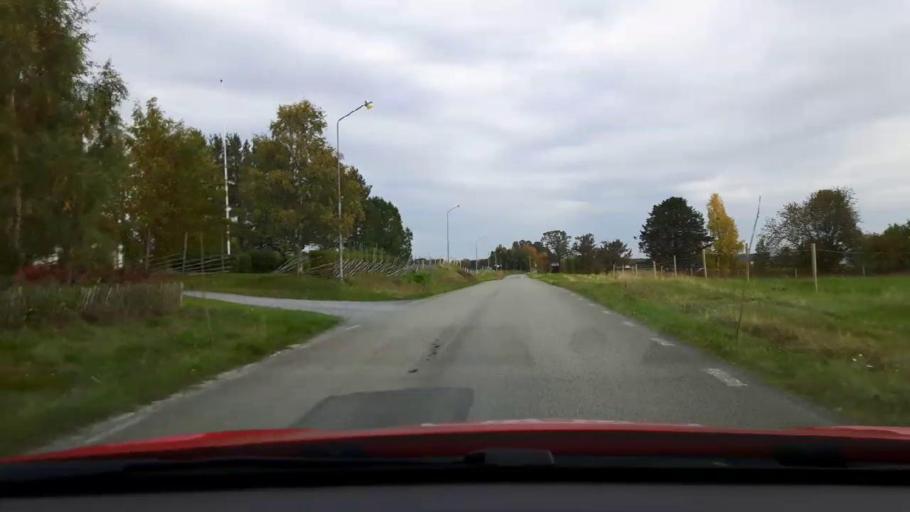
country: SE
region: Jaemtland
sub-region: Krokoms Kommun
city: Valla
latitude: 63.2533
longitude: 14.0292
